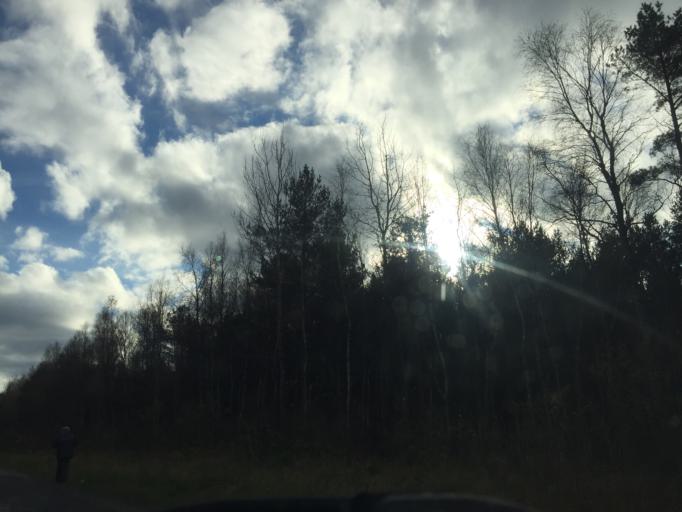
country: LV
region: Liepaja
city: Vec-Liepaja
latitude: 56.5661
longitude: 21.0547
